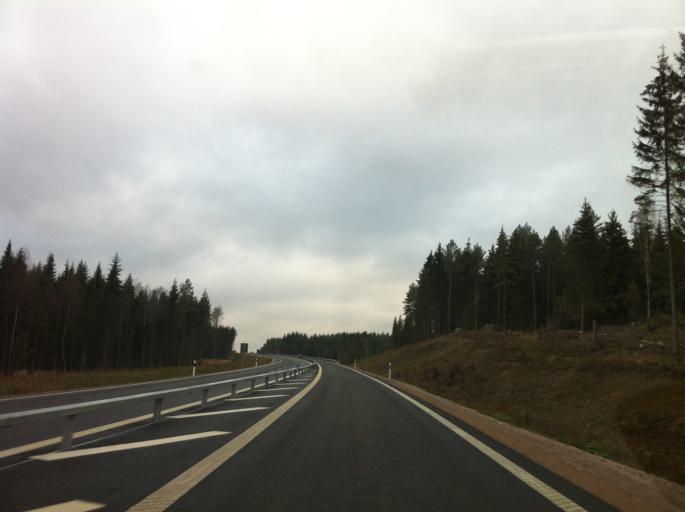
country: SE
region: Joenkoeping
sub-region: Vetlanda Kommun
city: Vetlanda
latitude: 57.4166
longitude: 15.2417
